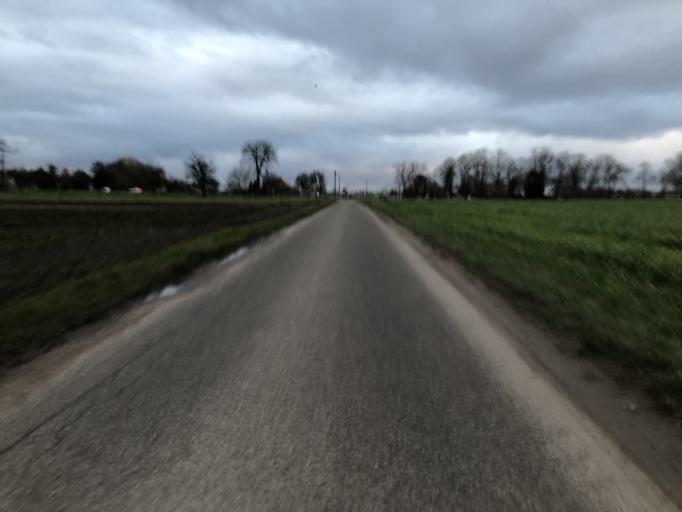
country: DE
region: Baden-Wuerttemberg
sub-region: Karlsruhe Region
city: Reilingen
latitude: 49.2931
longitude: 8.5831
